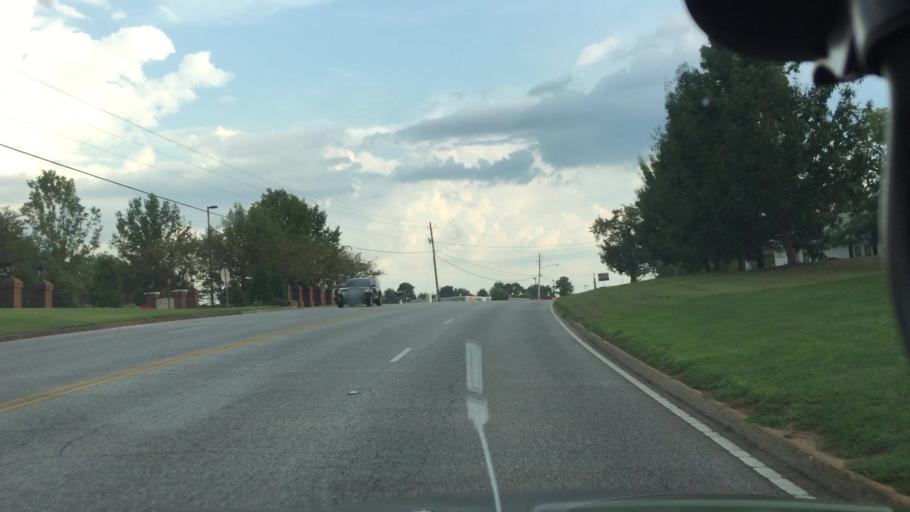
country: US
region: Alabama
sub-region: Coffee County
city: Enterprise
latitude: 31.3497
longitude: -85.8360
